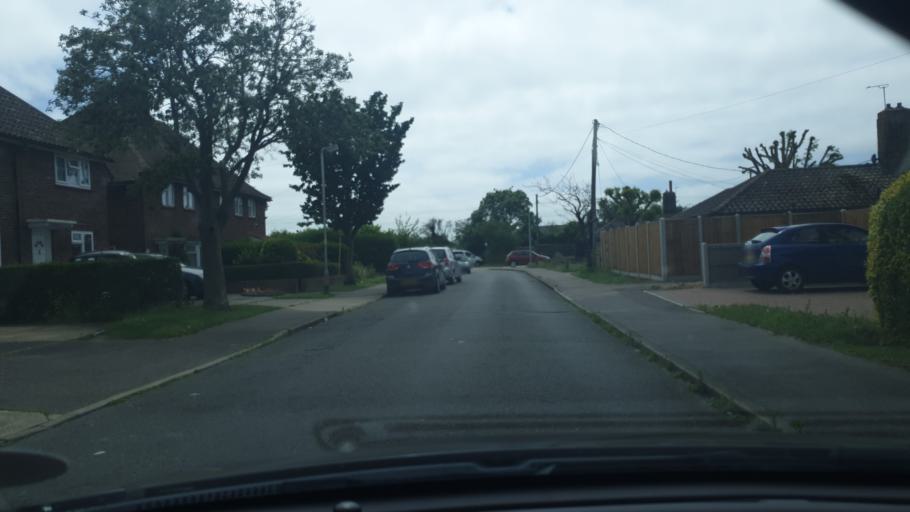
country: GB
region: England
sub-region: Essex
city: Frinton-on-Sea
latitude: 51.8412
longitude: 1.2215
